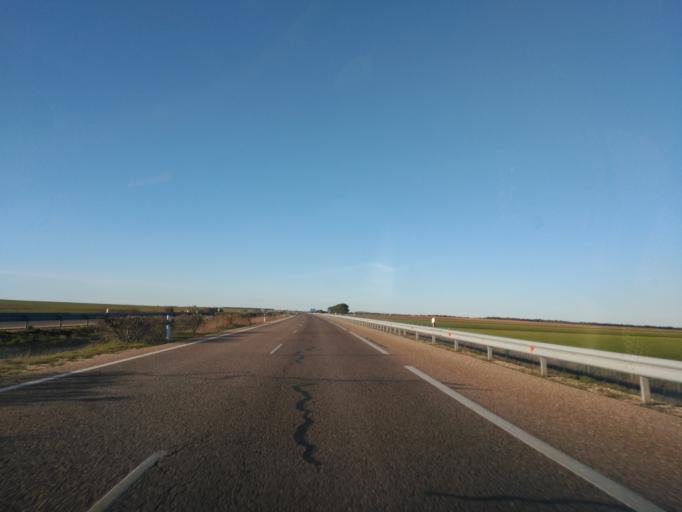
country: ES
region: Castille and Leon
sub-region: Provincia de Salamanca
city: Pajares de la Laguna
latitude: 41.1175
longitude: -5.4894
